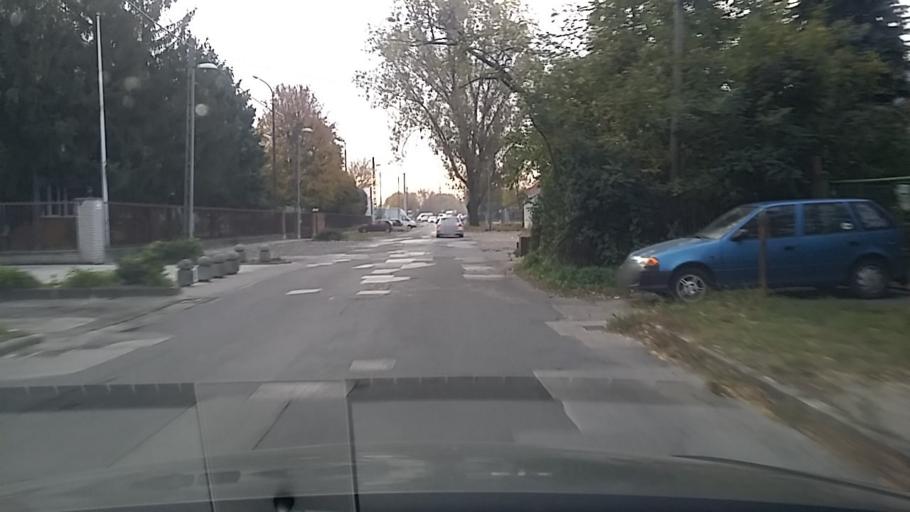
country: HU
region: Budapest
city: Budapest XV. keruelet
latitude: 47.5688
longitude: 19.1319
